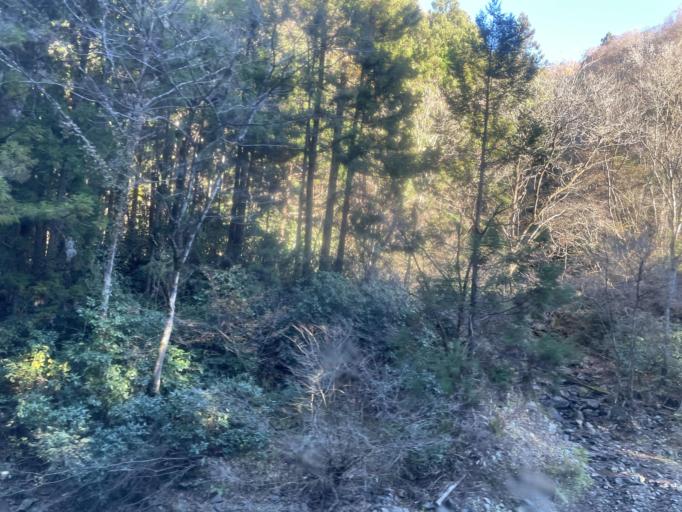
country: JP
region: Saitama
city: Yorii
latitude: 36.0255
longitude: 139.1718
